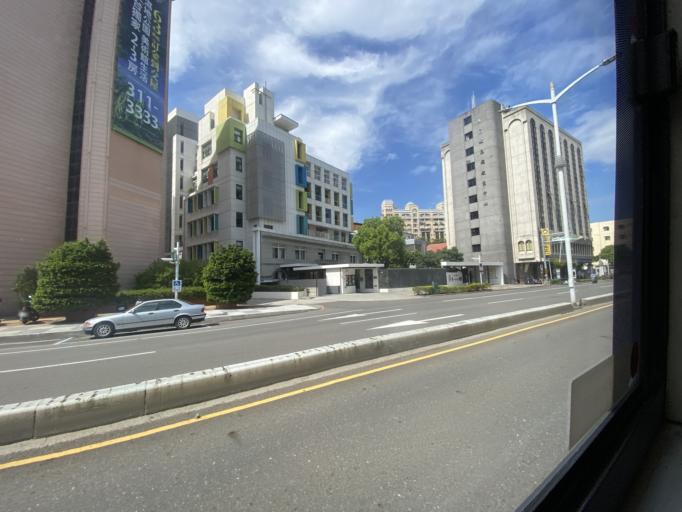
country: TW
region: Kaohsiung
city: Kaohsiung
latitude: 22.6205
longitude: 120.2926
